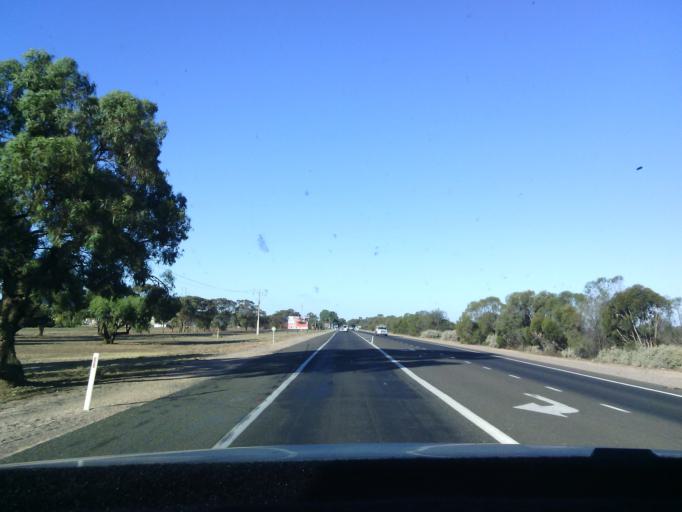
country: AU
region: South Australia
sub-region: Renmark Paringa
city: Renmark West
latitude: -34.2121
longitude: 140.6957
